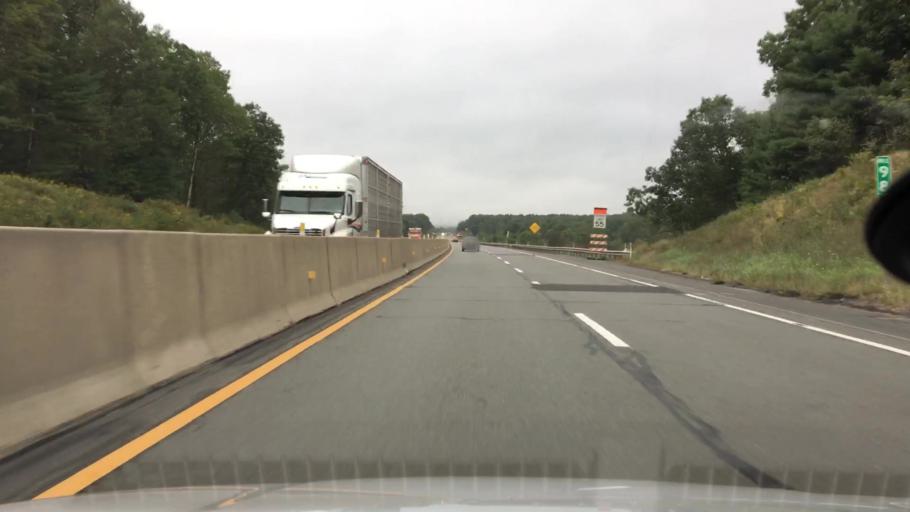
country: US
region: Pennsylvania
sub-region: Luzerne County
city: White Haven
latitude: 41.1105
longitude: -75.7557
